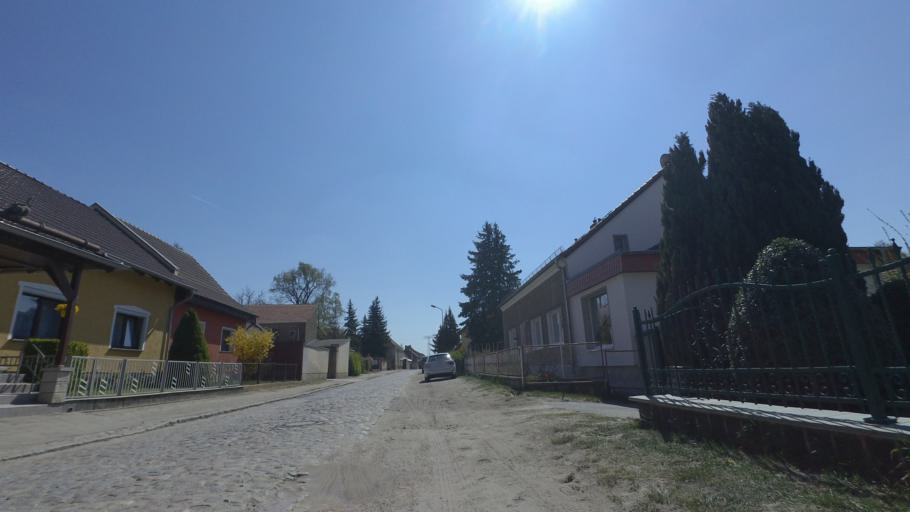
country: DE
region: Brandenburg
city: Zossen
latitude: 52.2095
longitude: 13.4664
